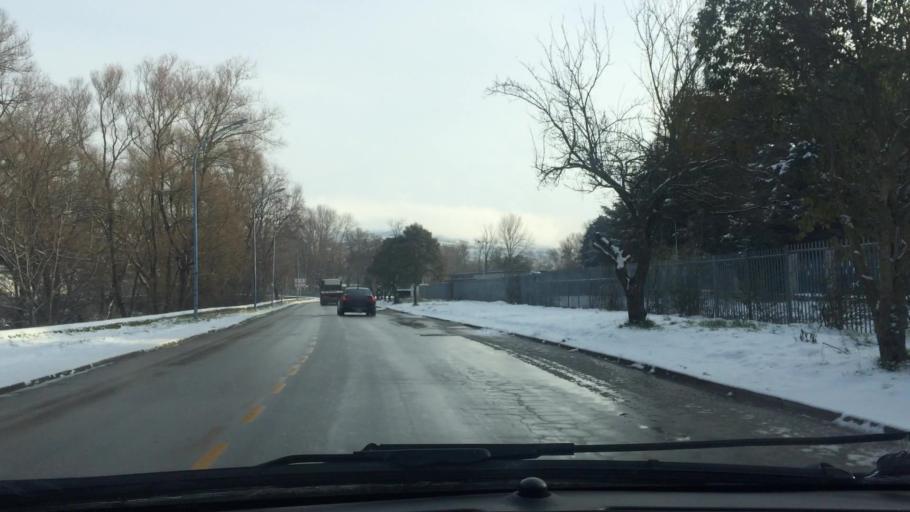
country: IT
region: Basilicate
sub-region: Provincia di Potenza
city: Potenza
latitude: 40.6323
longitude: 15.8160
